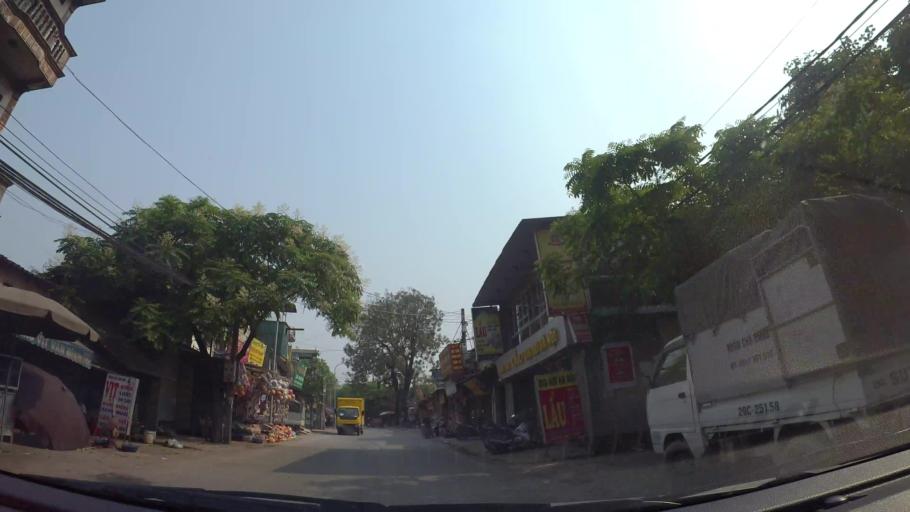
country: VN
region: Ha Noi
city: Ha Dong
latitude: 20.9987
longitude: 105.7516
